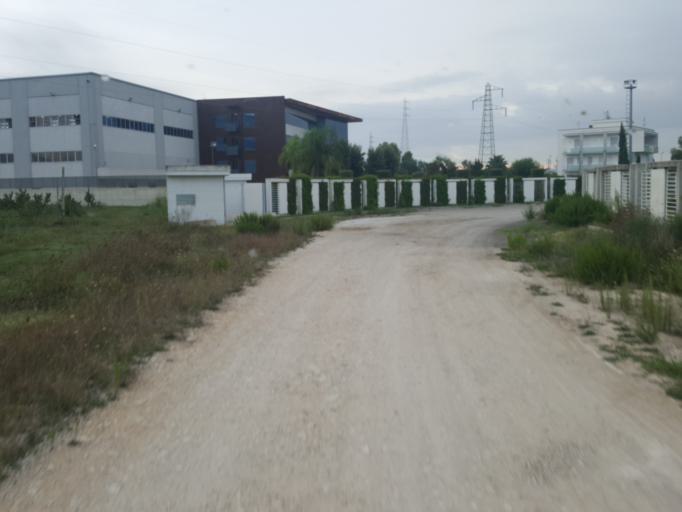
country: IT
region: Campania
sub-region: Provincia di Caserta
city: Pignataro Maggiore
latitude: 41.1722
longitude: 14.1557
